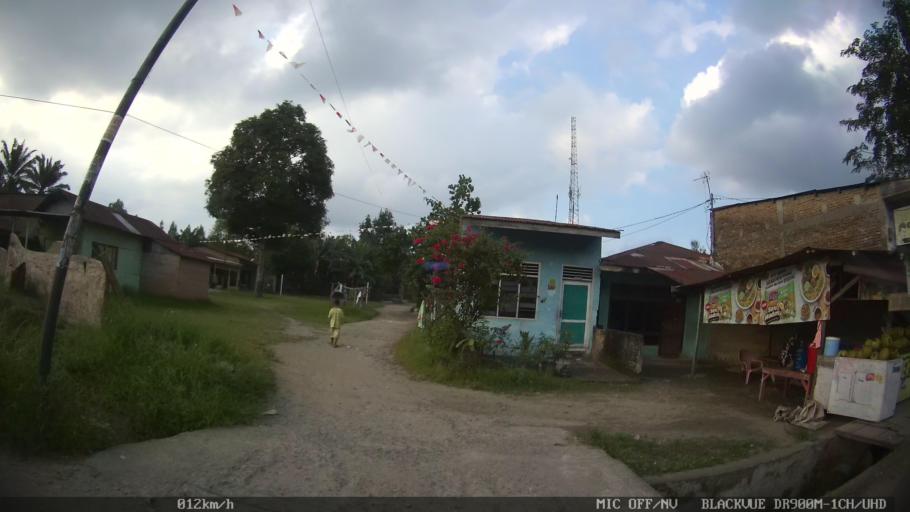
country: ID
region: North Sumatra
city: Medan
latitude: 3.5852
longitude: 98.7361
